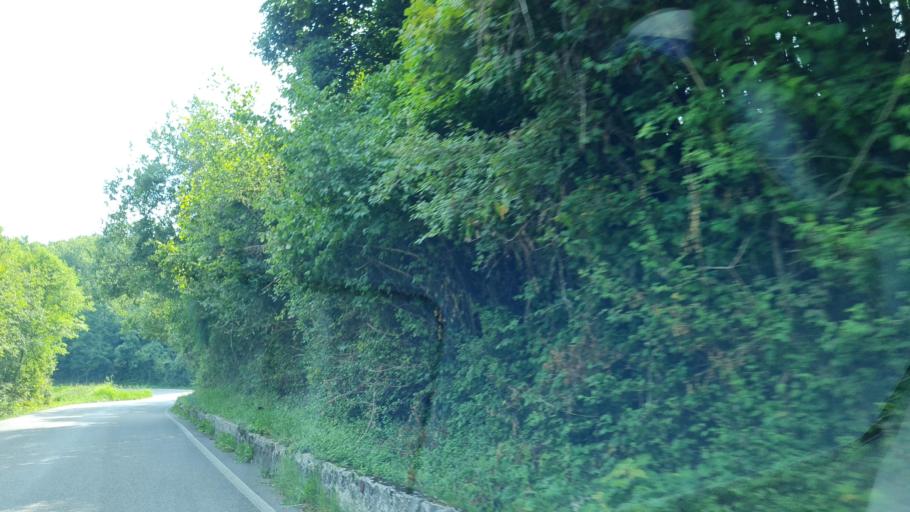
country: IT
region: Veneto
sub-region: Provincia di Vicenza
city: Conco
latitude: 45.8030
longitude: 11.6256
